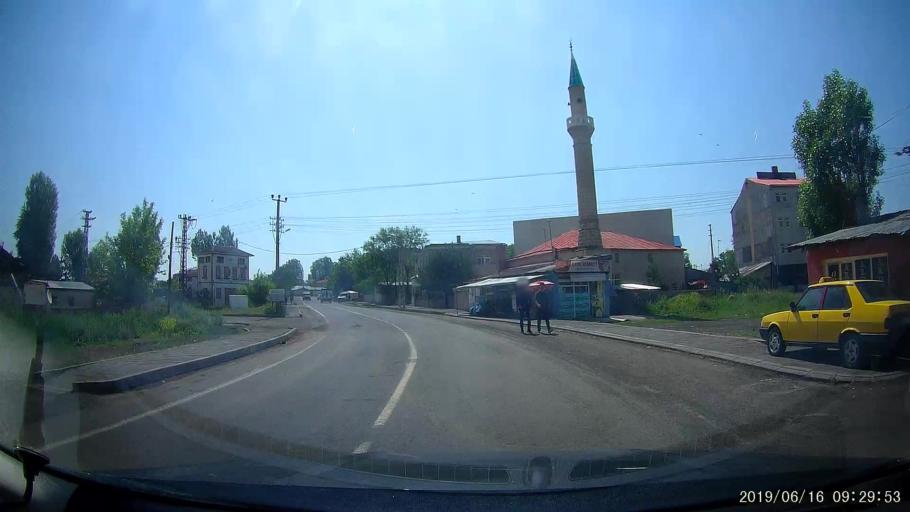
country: TR
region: Kars
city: Kars
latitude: 40.6011
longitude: 43.1048
